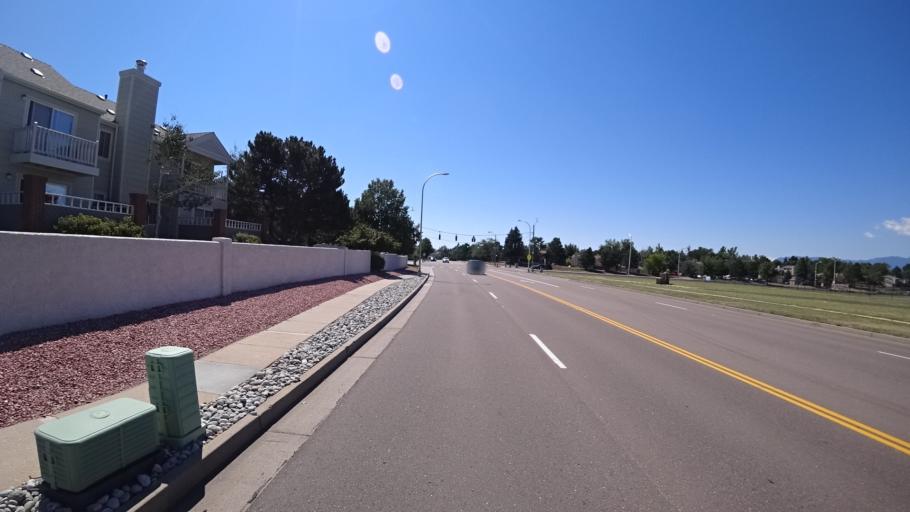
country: US
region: Colorado
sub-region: El Paso County
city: Black Forest
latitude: 38.9493
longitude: -104.7702
